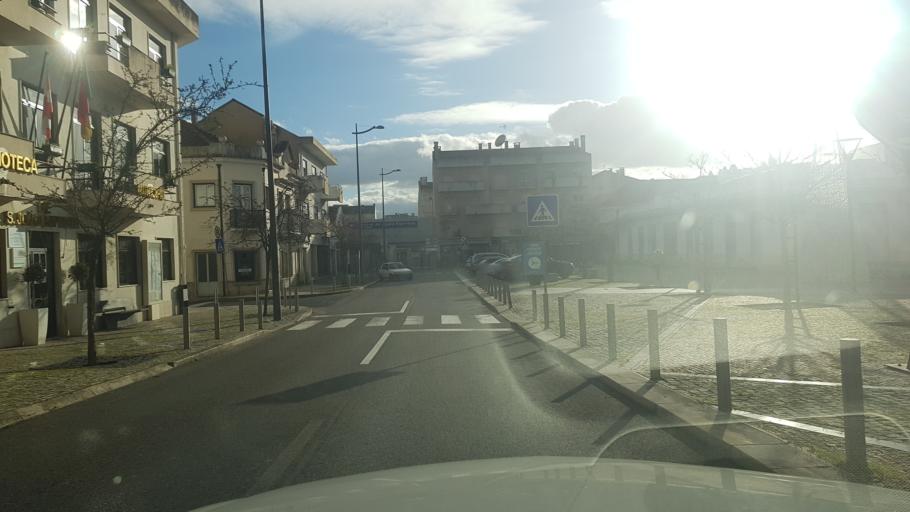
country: PT
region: Santarem
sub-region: Entroncamento
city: Entroncamento
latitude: 39.4651
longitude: -8.4679
